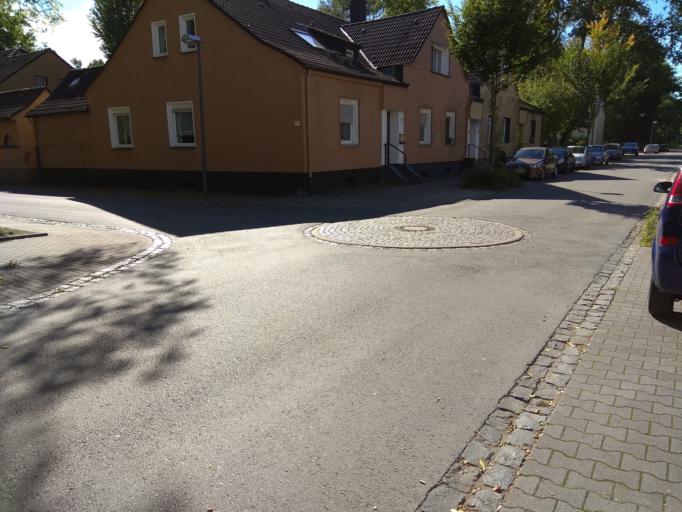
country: DE
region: North Rhine-Westphalia
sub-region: Regierungsbezirk Munster
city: Gelsenkirchen
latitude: 51.5430
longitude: 7.1041
